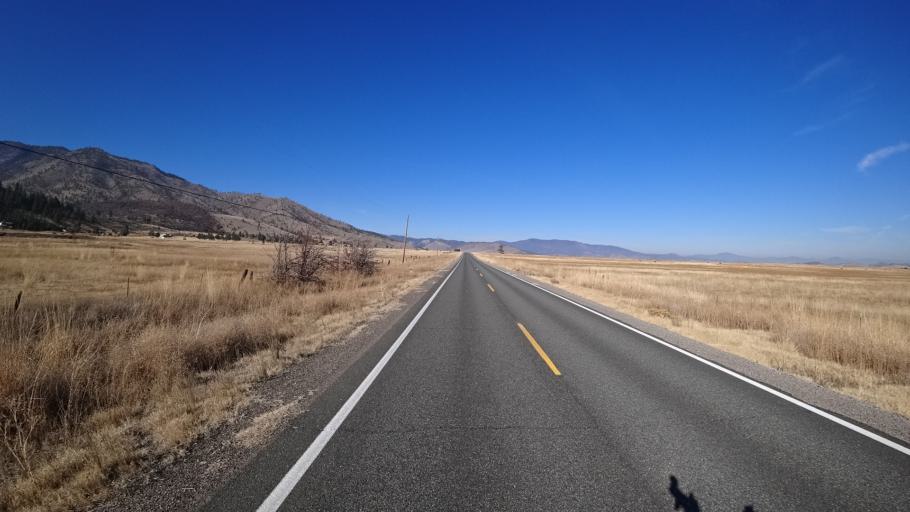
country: US
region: California
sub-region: Siskiyou County
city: Weed
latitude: 41.4719
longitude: -122.4800
